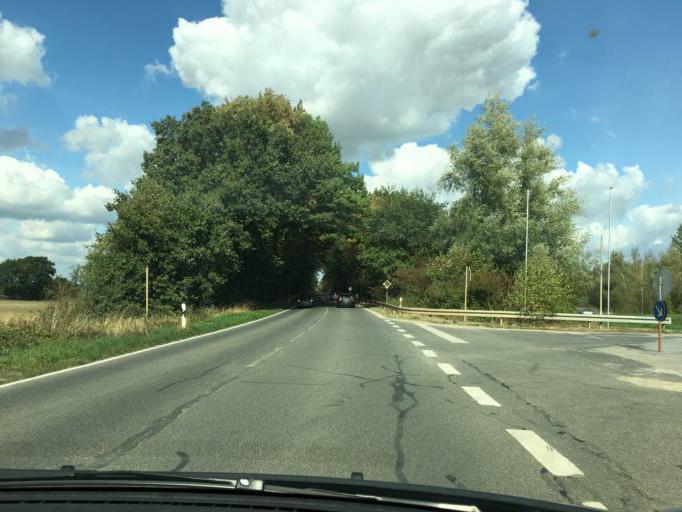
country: DE
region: North Rhine-Westphalia
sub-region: Regierungsbezirk Koln
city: Elsdorf
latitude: 50.8909
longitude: 6.6100
